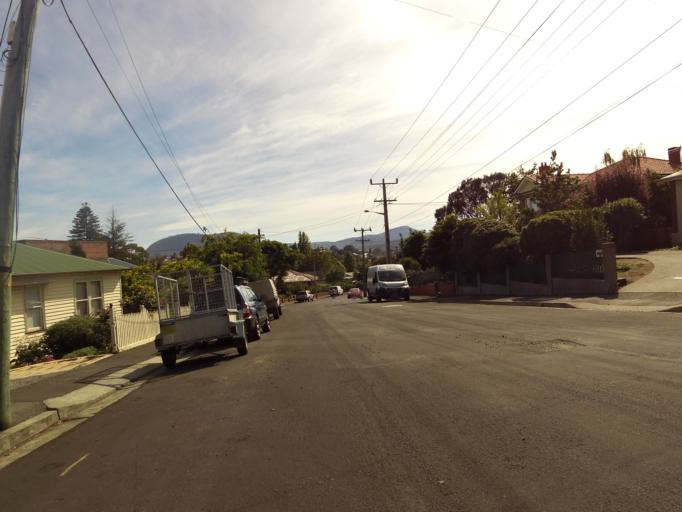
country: AU
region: Tasmania
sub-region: Hobart
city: New Town
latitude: -42.8535
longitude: 147.3104
